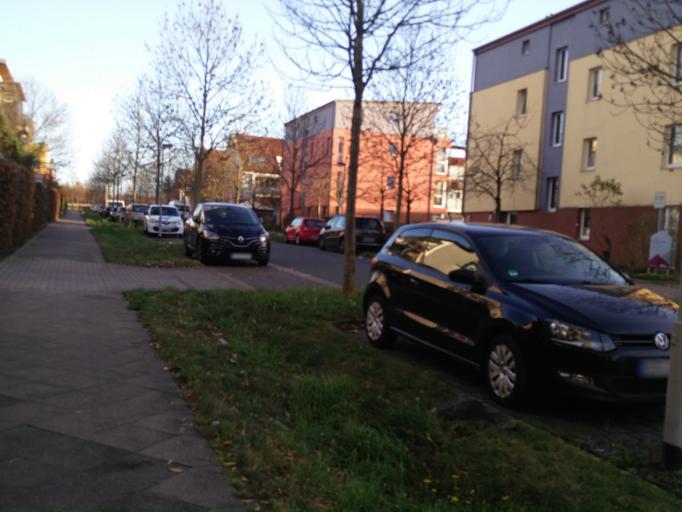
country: DE
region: Lower Saxony
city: Laatzen
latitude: 52.3338
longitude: 9.8345
